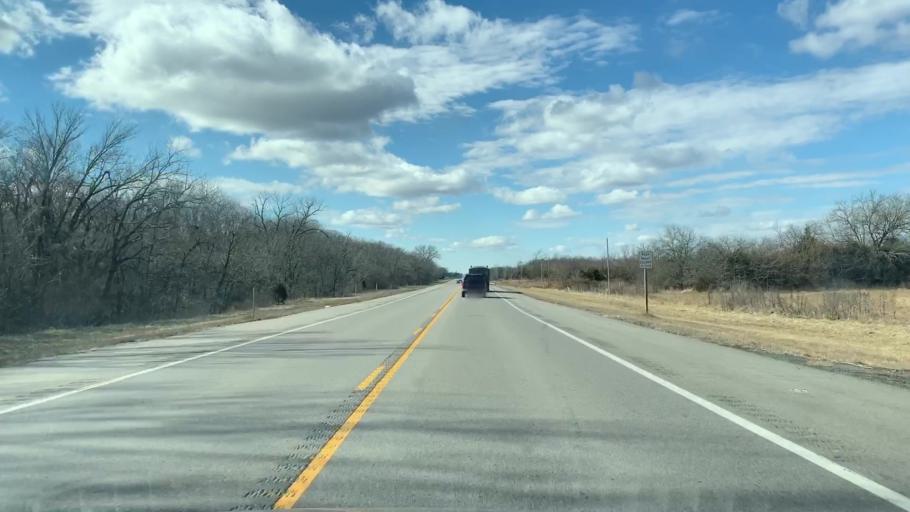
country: US
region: Kansas
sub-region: Cherokee County
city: Columbus
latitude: 37.3400
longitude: -94.9262
